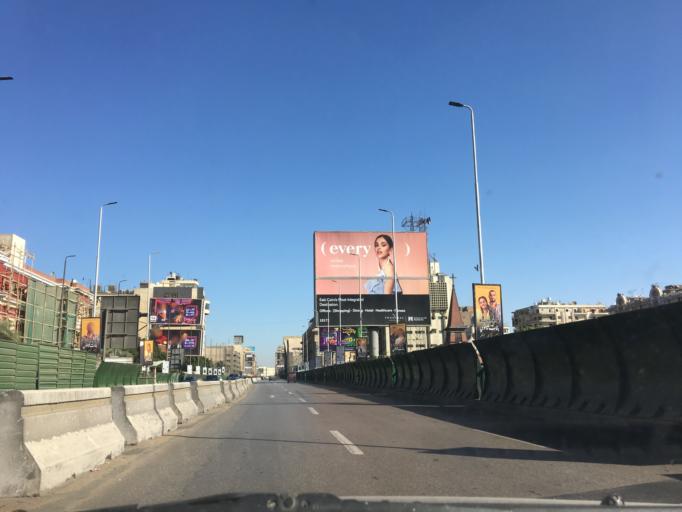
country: EG
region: Muhafazat al Qahirah
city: Cairo
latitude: 30.0537
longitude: 31.2377
